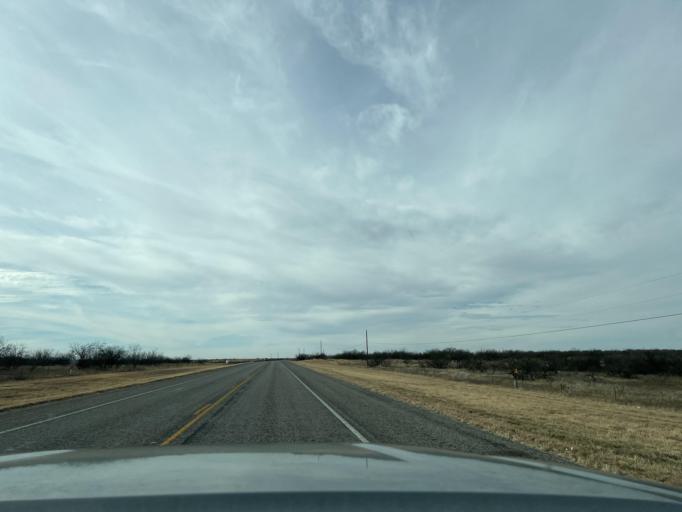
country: US
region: Texas
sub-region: Shackelford County
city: Albany
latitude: 32.7101
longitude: -99.4393
